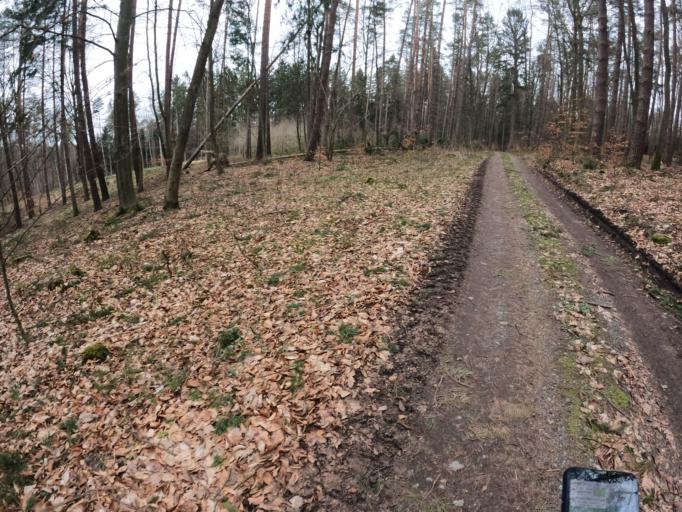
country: PL
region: West Pomeranian Voivodeship
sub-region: Powiat kamienski
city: Golczewo
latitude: 53.8157
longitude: 15.0264
